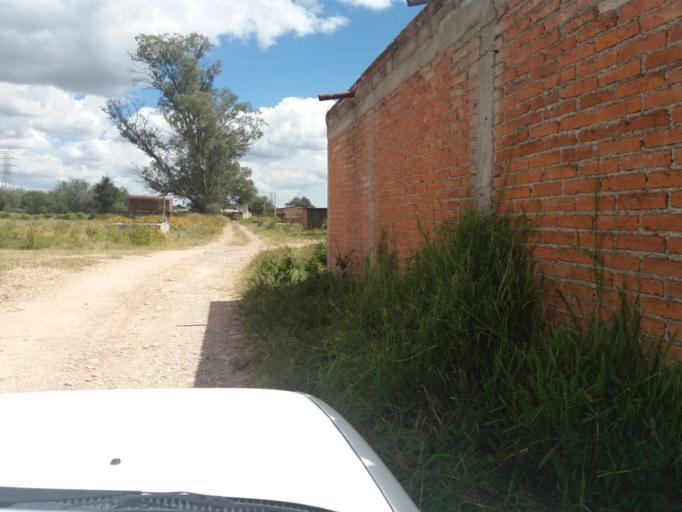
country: MX
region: Aguascalientes
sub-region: Aguascalientes
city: San Sebastian [Fraccionamiento]
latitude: 21.8172
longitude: -102.2711
